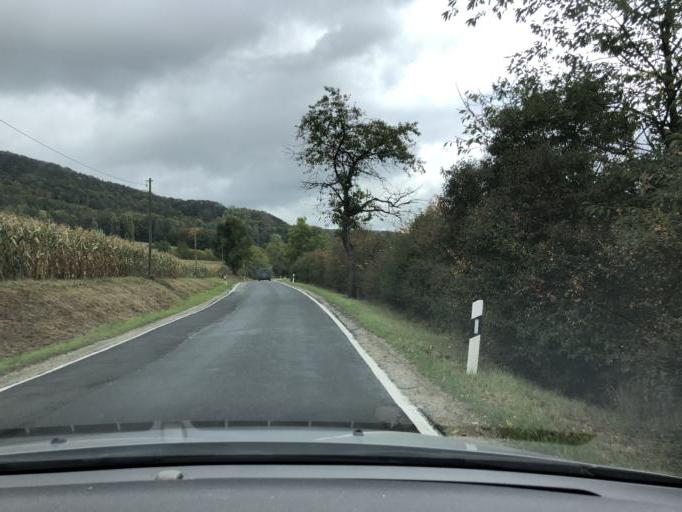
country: DE
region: Thuringia
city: Grossbartloff
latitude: 51.2395
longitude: 10.2063
